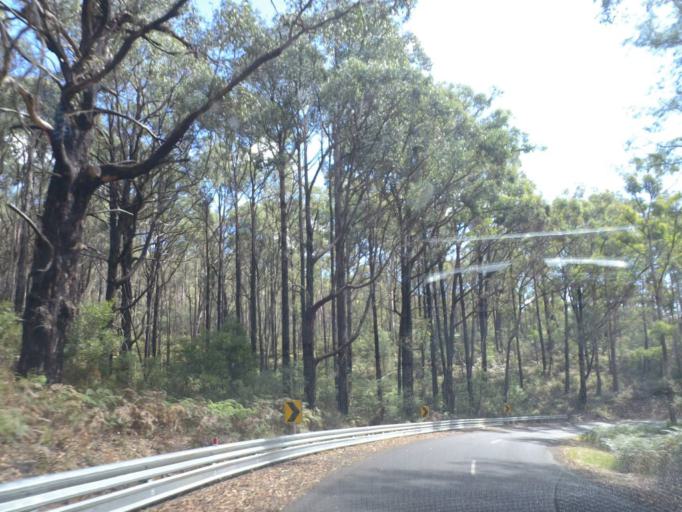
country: AU
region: Victoria
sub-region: Murrindindi
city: Alexandra
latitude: -37.3361
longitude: 145.9473
